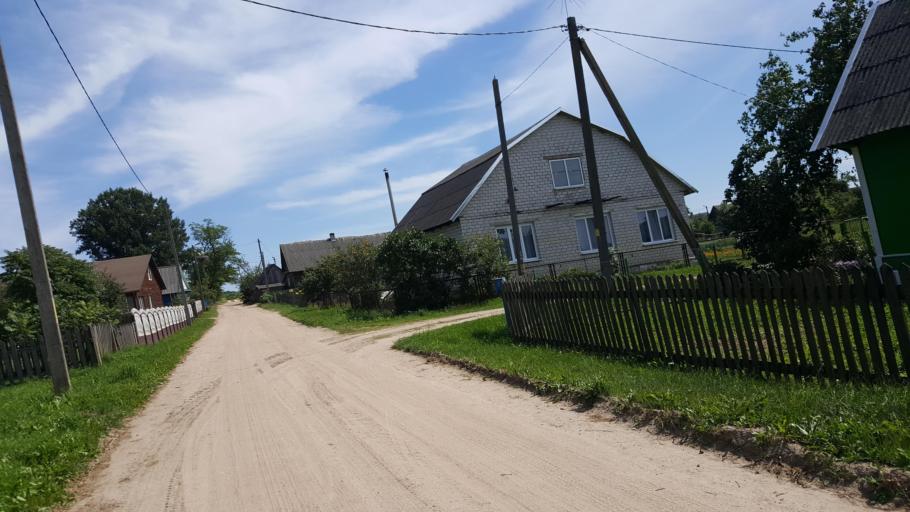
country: BY
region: Brest
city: Pruzhany
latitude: 52.5506
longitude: 24.2233
